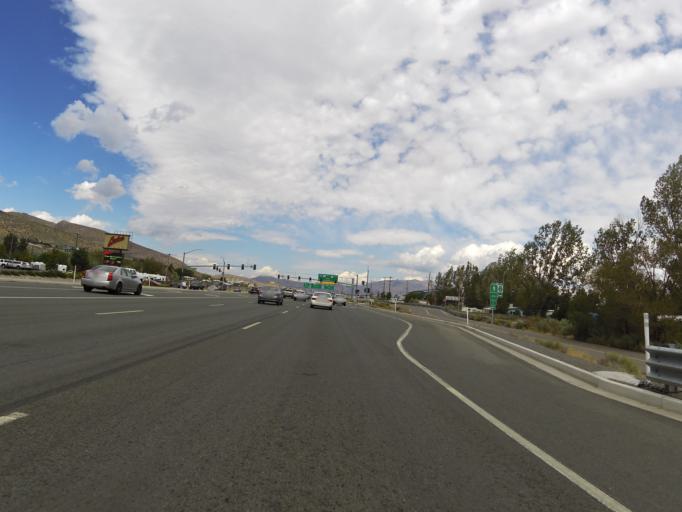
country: US
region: Nevada
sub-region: Douglas County
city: Indian Hills
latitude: 39.1154
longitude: -119.7727
